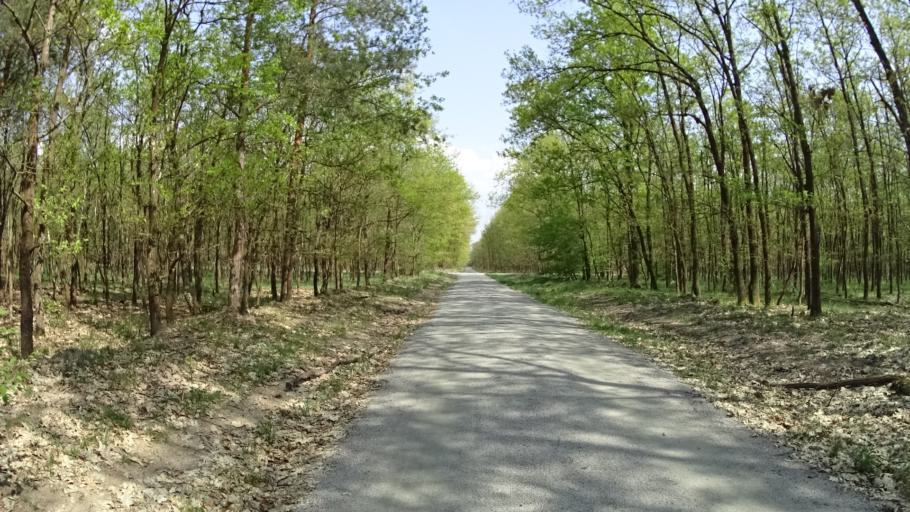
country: DE
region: Hesse
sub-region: Regierungsbezirk Darmstadt
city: Einhausen
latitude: 49.6556
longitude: 8.5105
